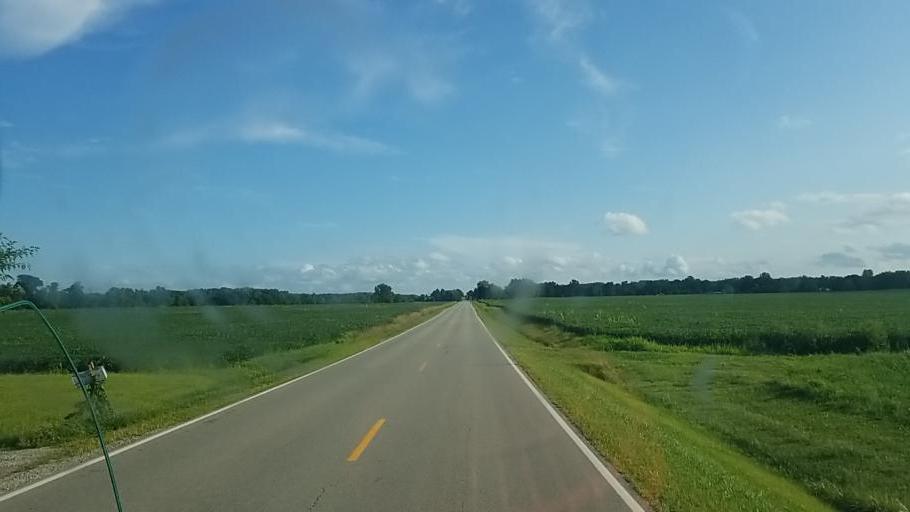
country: US
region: Ohio
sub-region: Crawford County
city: Bucyrus
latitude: 40.8119
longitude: -83.0930
